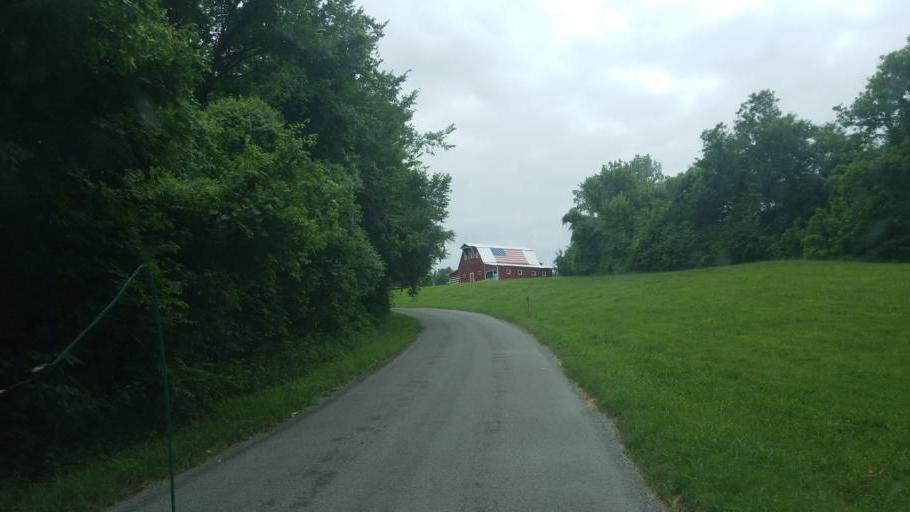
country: US
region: Illinois
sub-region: Jackson County
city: Murphysboro
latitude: 37.6902
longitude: -89.3878
